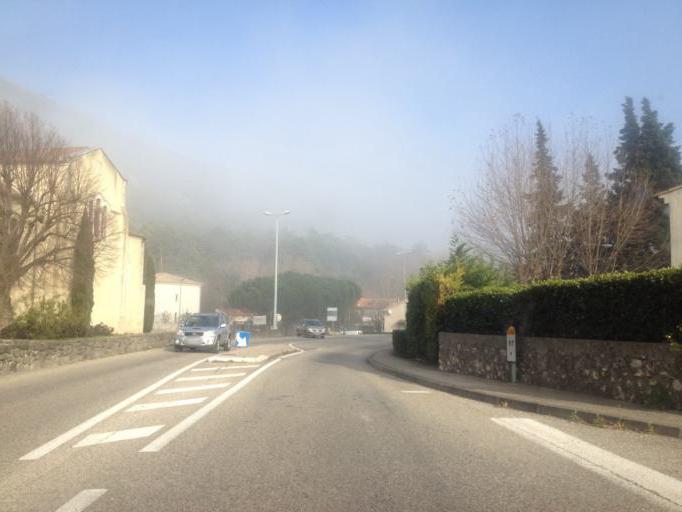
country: FR
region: Rhone-Alpes
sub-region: Departement de l'Ardeche
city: Rochemaure
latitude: 44.5887
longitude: 4.7054
